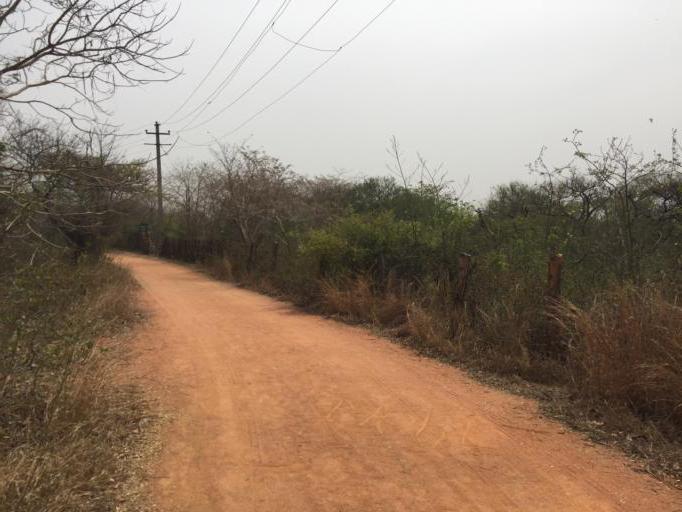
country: IN
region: NCT
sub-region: Central Delhi
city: Karol Bagh
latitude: 28.5581
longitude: 77.1489
